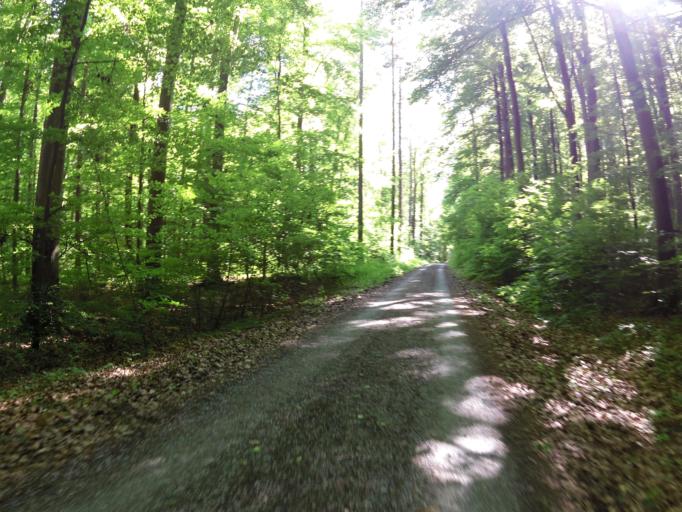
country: DE
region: Bavaria
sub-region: Regierungsbezirk Unterfranken
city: Reichenberg
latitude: 49.7502
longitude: 9.9059
